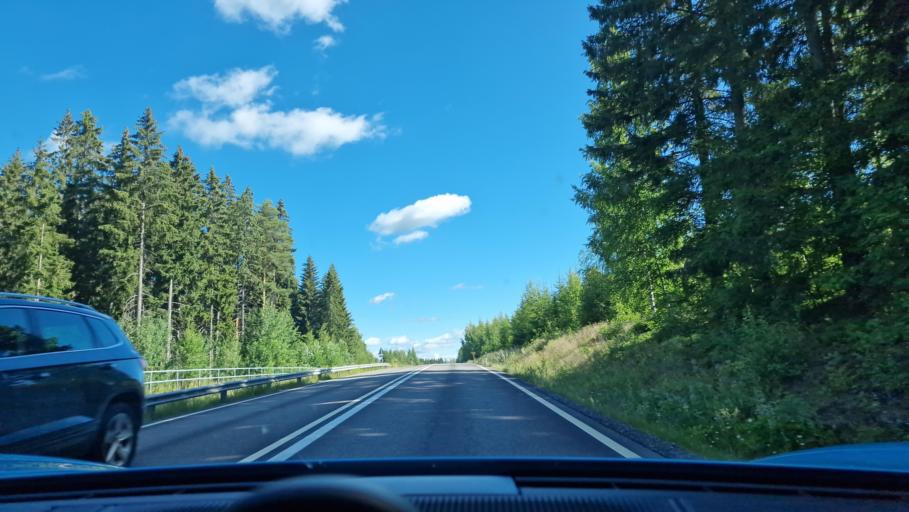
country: FI
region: Pirkanmaa
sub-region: Tampere
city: Kangasala
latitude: 61.4645
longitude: 24.1249
